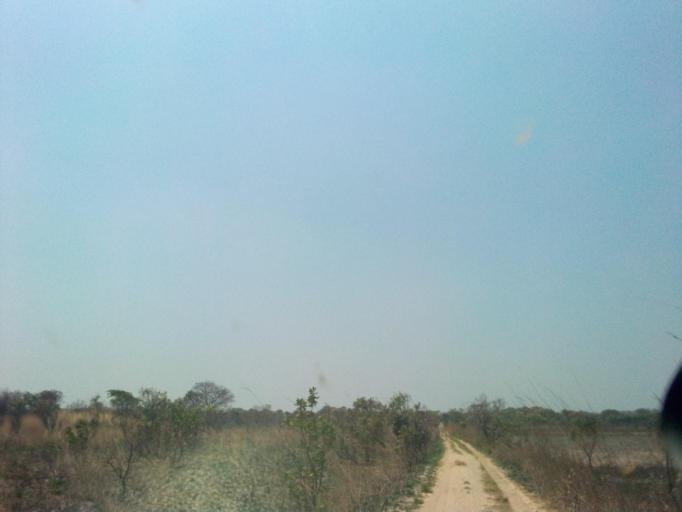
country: ZM
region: Copperbelt
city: Kataba
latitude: -12.2478
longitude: 30.3941
